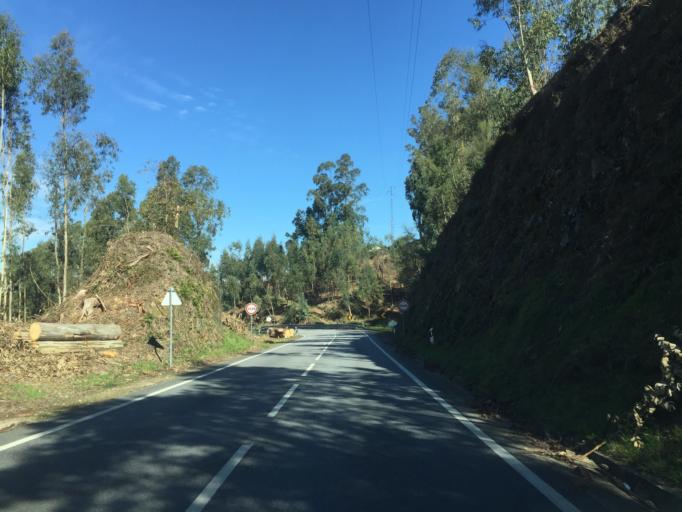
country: PT
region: Aveiro
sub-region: Vale de Cambra
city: Macieira de Cambra
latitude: 40.9043
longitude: -8.3283
